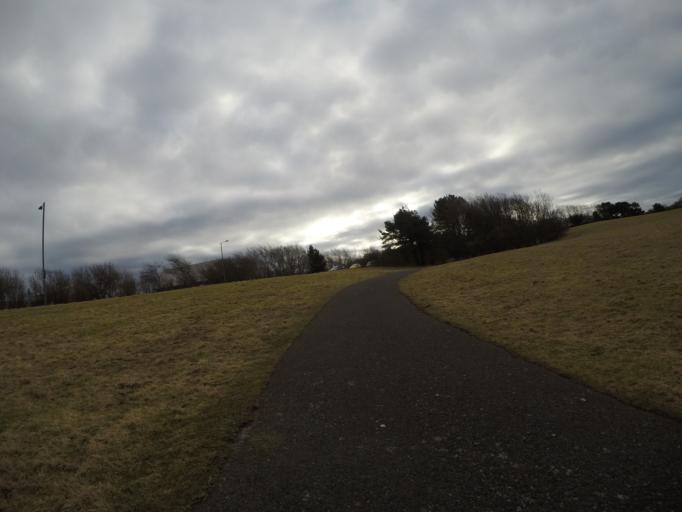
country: GB
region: Scotland
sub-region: North Ayrshire
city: Irvine
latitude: 55.6058
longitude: -4.6814
